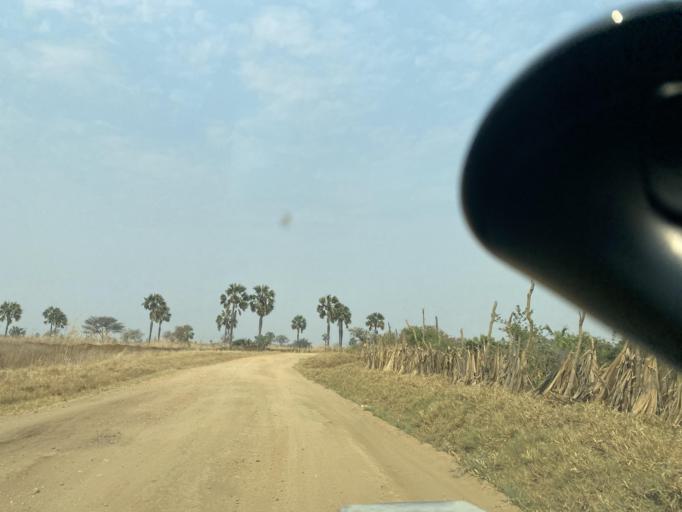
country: ZM
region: Lusaka
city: Kafue
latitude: -15.6506
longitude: 28.0658
